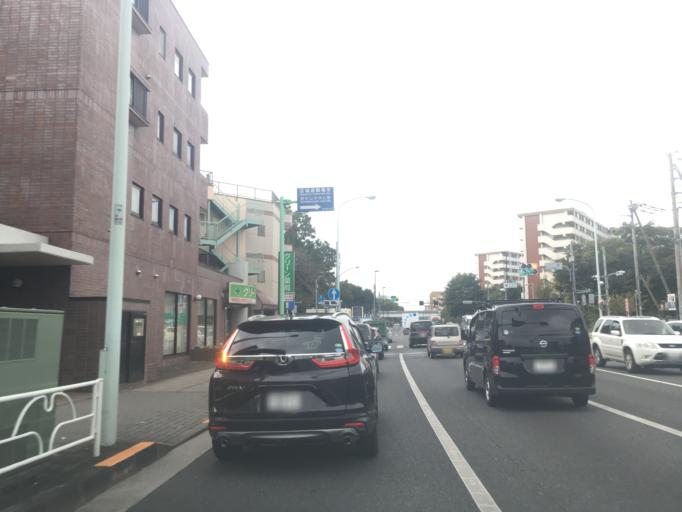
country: JP
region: Tokyo
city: Higashimurayama-shi
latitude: 35.7447
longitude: 139.4670
